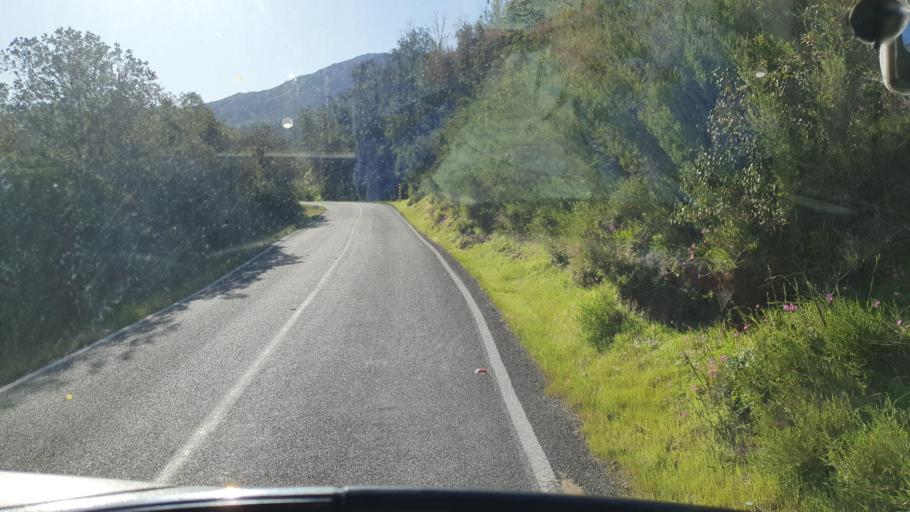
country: CL
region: Valparaiso
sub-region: Provincia de Marga Marga
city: Limache
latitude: -33.1813
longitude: -71.1784
